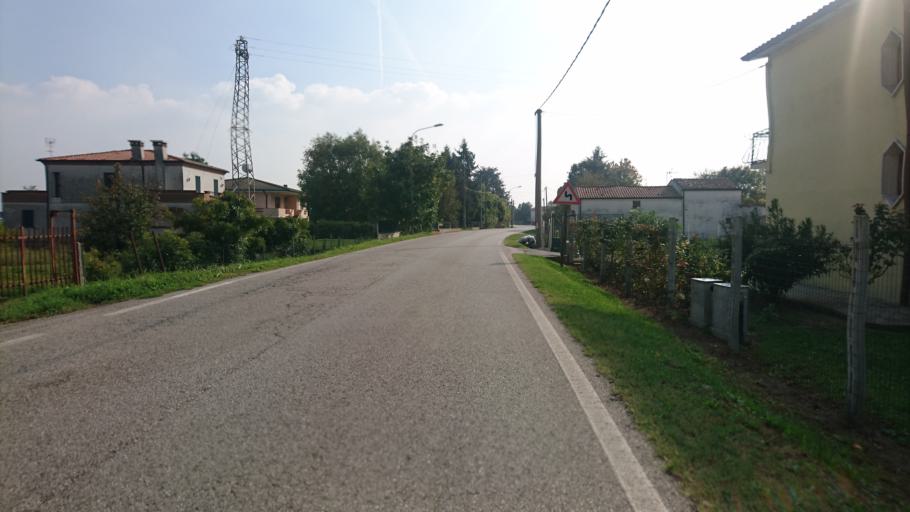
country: IT
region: Veneto
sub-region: Provincia di Rovigo
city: Grignano Polesine
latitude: 45.0375
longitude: 11.7525
